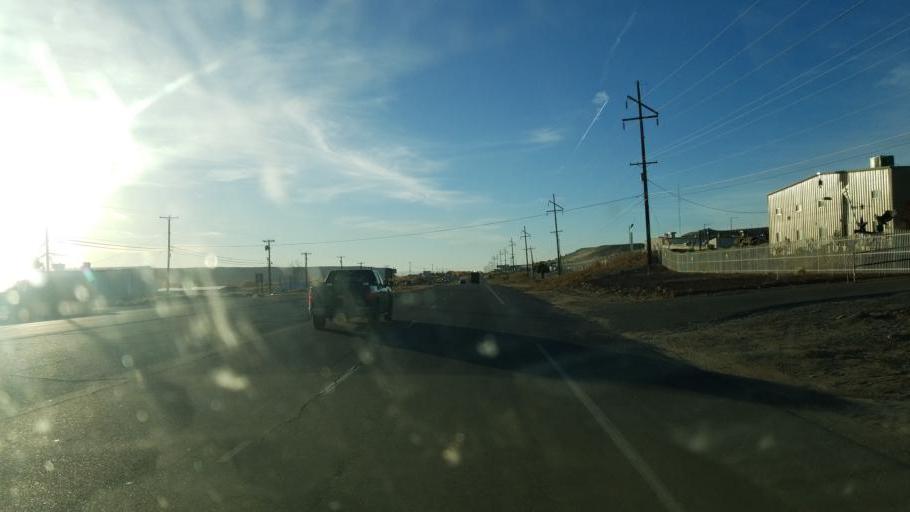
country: US
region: New Mexico
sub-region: San Juan County
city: Lee Acres
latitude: 36.7040
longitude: -108.1048
